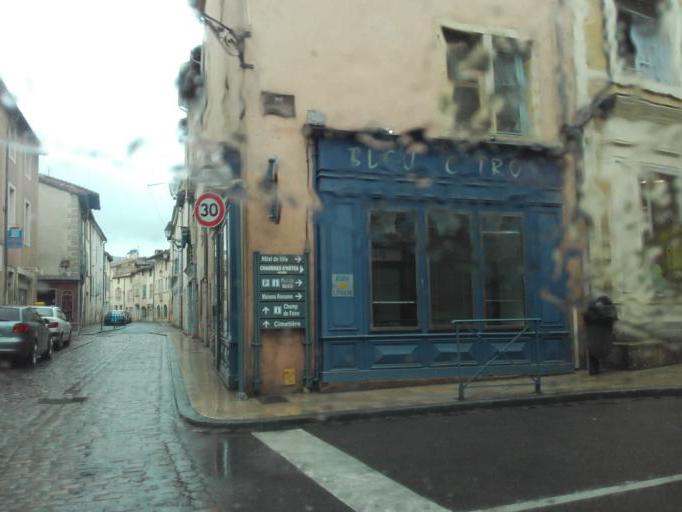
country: FR
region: Bourgogne
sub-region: Departement de Saone-et-Loire
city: Cluny
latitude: 46.4348
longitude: 4.6565
